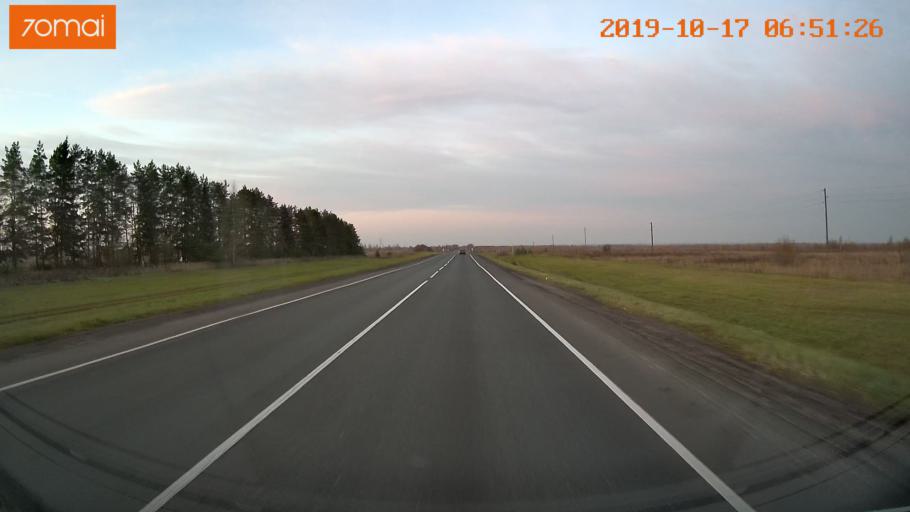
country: RU
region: Vladimir
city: Kideksha
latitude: 56.4956
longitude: 40.5273
